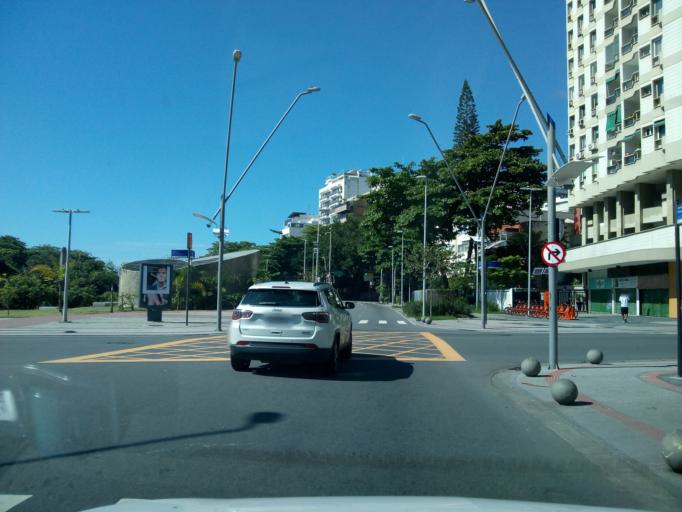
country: BR
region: Rio de Janeiro
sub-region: Rio De Janeiro
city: Rio de Janeiro
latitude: -22.9835
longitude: -43.2157
